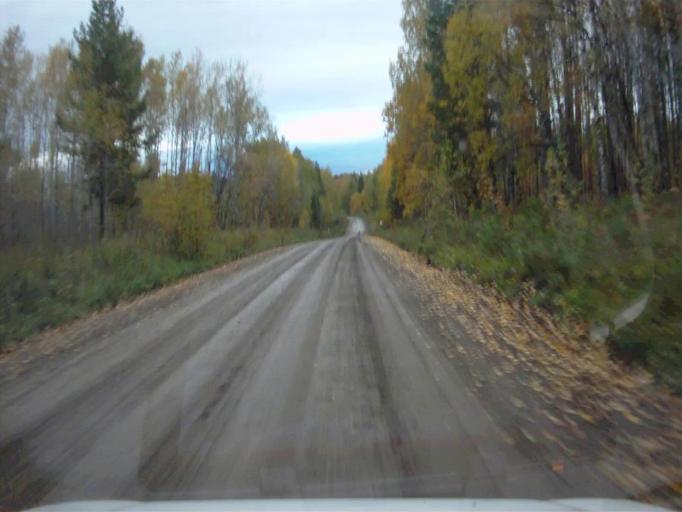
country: RU
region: Chelyabinsk
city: Nyazepetrovsk
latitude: 56.1167
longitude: 59.3682
